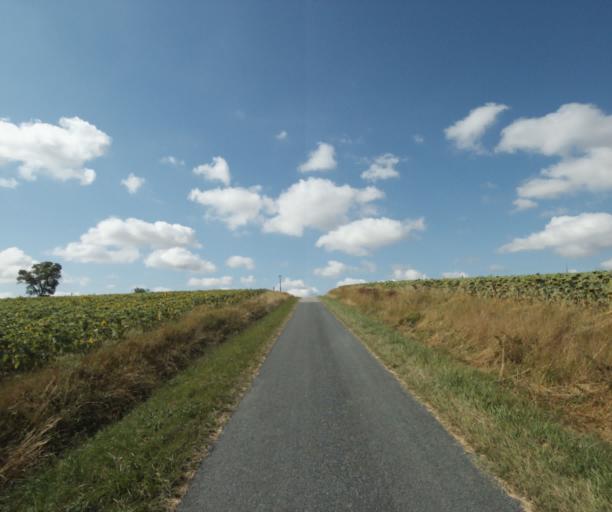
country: FR
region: Midi-Pyrenees
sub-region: Departement de la Haute-Garonne
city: Avignonet-Lauragais
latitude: 43.4419
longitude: 1.7960
